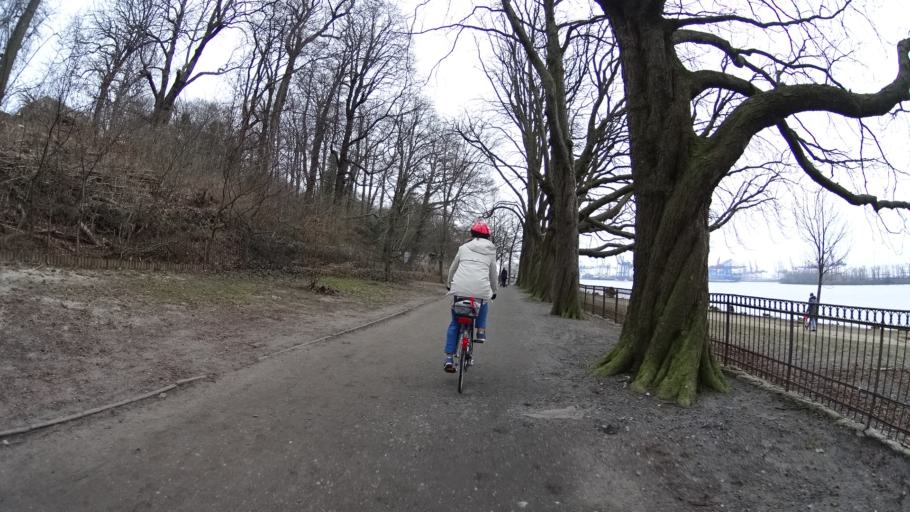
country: DE
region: Hamburg
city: Altona
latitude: 53.5450
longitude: 9.8908
